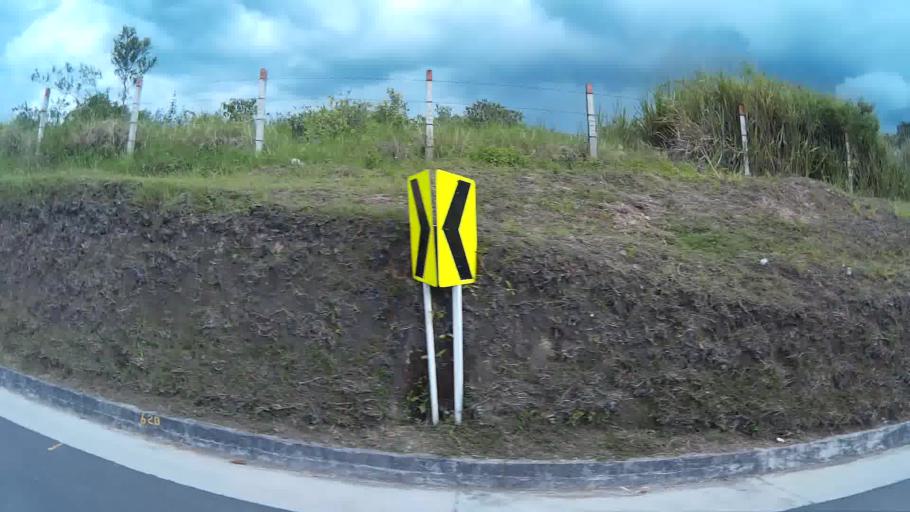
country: CO
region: Risaralda
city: Pereira
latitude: 4.7969
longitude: -75.7551
